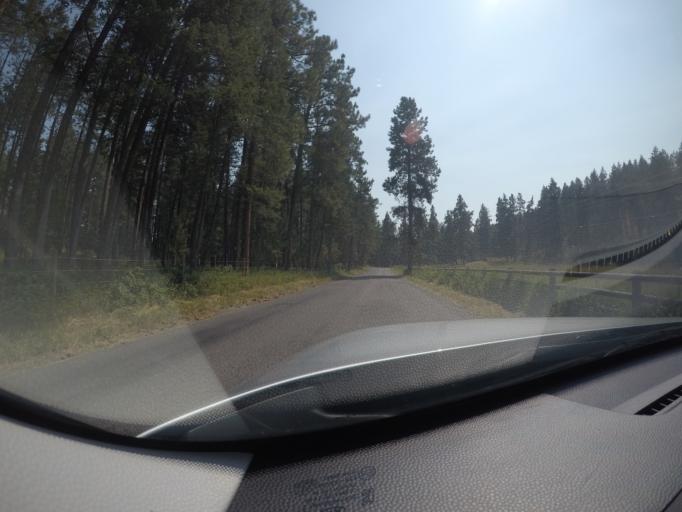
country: US
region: Montana
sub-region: Lake County
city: Polson
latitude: 47.7709
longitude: -114.1510
